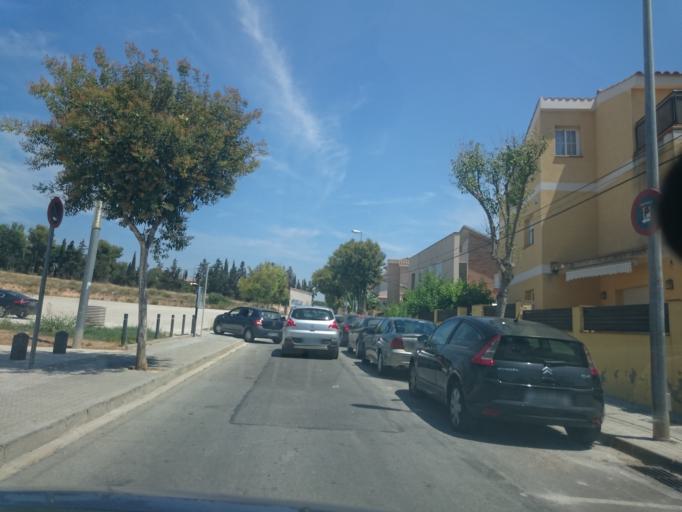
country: ES
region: Catalonia
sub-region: Provincia de Barcelona
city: Vilanova i la Geltru
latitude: 41.2258
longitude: 1.6960
